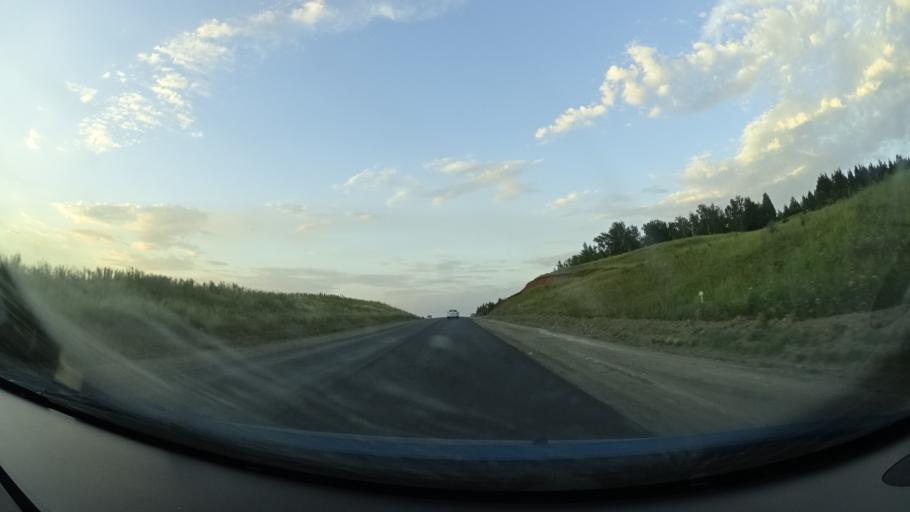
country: RU
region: Orenburg
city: Severnoye
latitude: 54.1713
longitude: 52.6456
